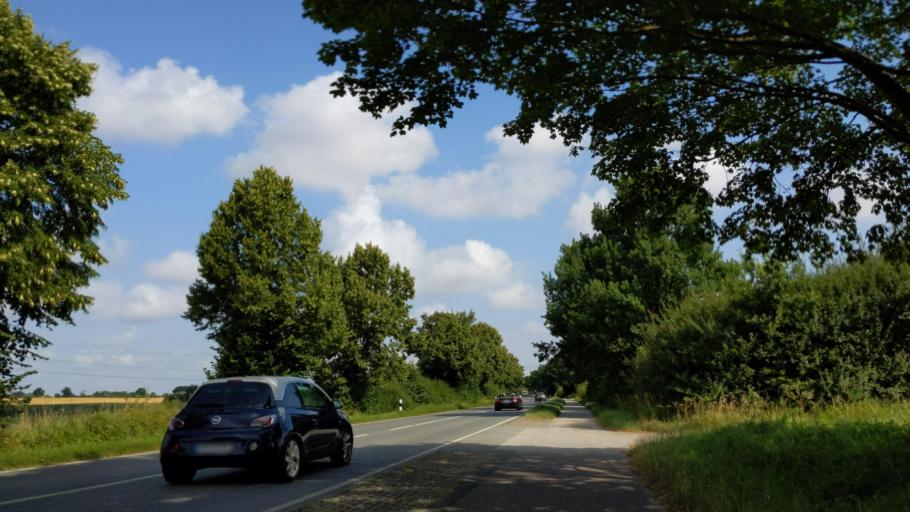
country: DE
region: Schleswig-Holstein
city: Stockelsdorf
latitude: 53.9175
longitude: 10.6397
